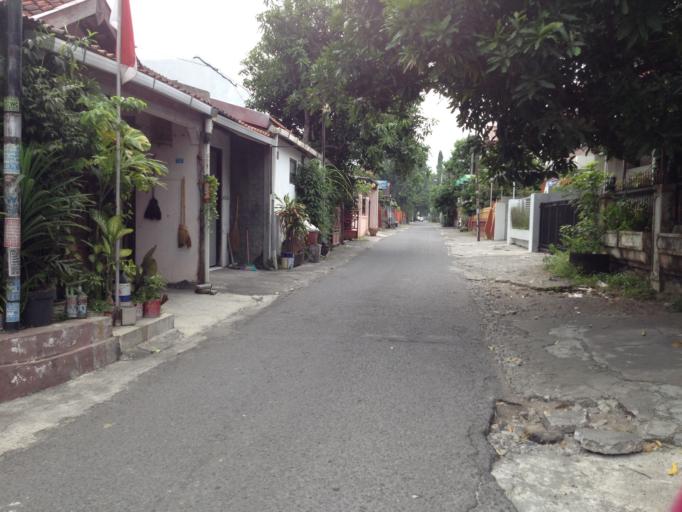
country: ID
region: Daerah Istimewa Yogyakarta
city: Yogyakarta
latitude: -7.8138
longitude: 110.4002
